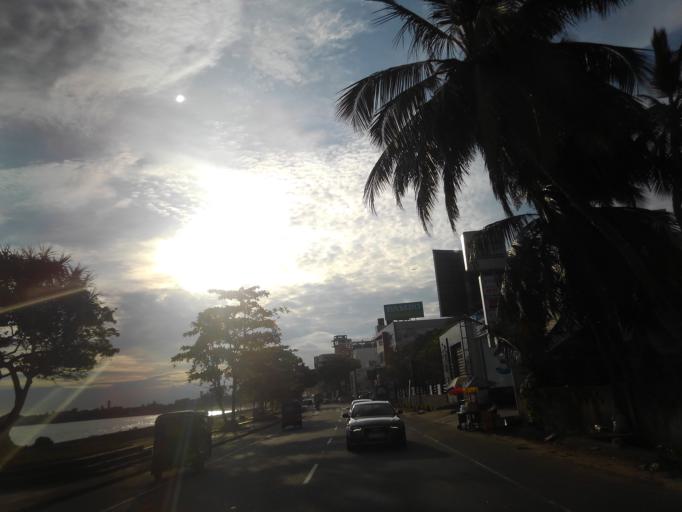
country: LK
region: Southern
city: Galle
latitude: 6.0370
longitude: 80.2246
